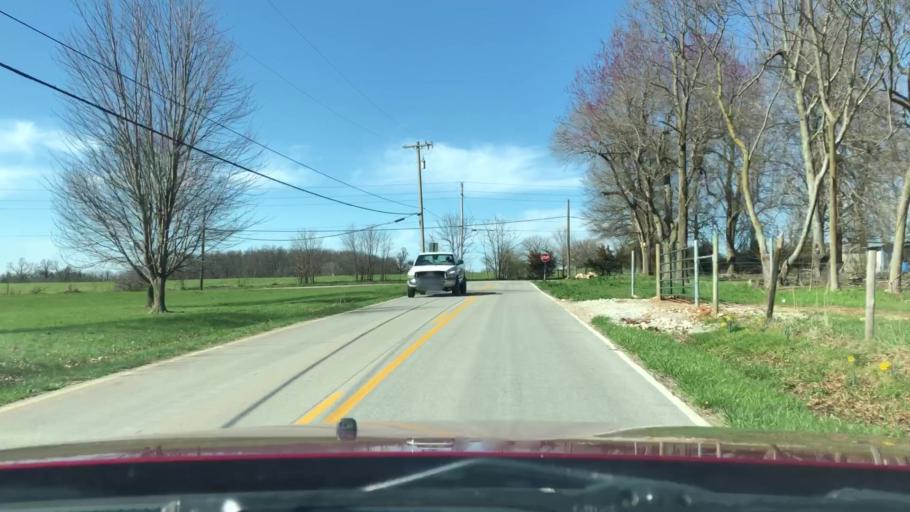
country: US
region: Missouri
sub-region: Greene County
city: Strafford
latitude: 37.2375
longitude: -93.1882
